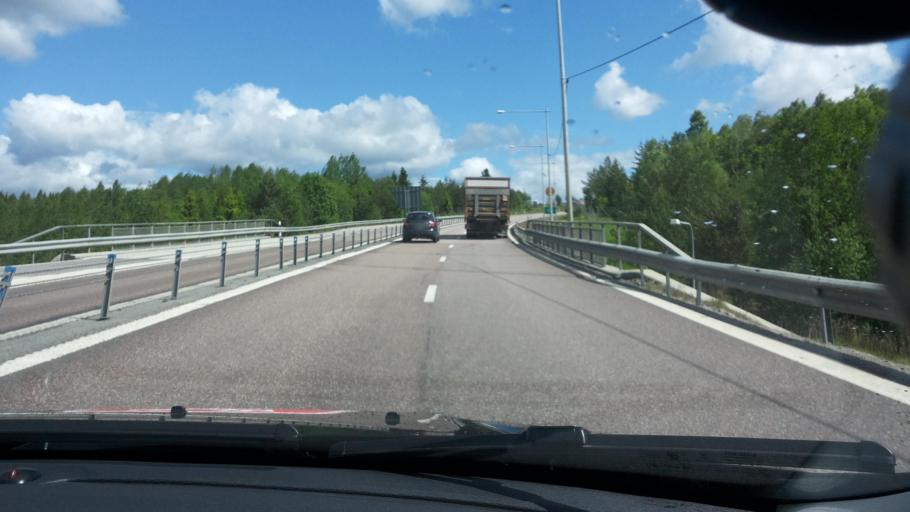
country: SE
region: Vaesternorrland
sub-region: Timra Kommun
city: Soraker
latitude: 62.5258
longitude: 17.4755
